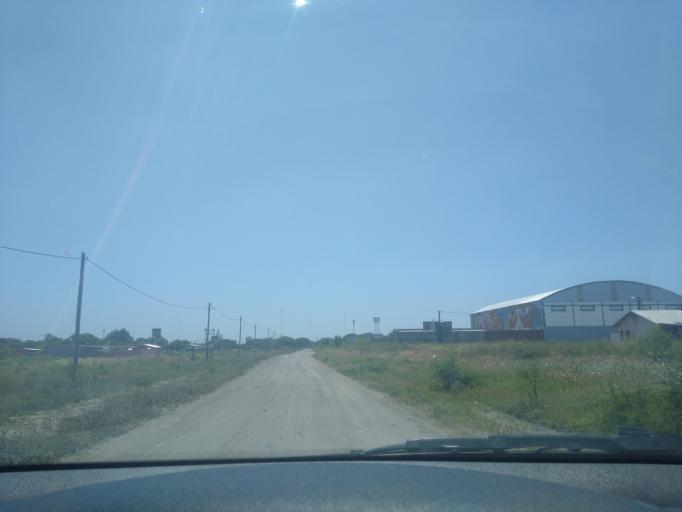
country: AR
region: Chaco
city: Puerto Tirol
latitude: -27.3800
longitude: -59.0946
